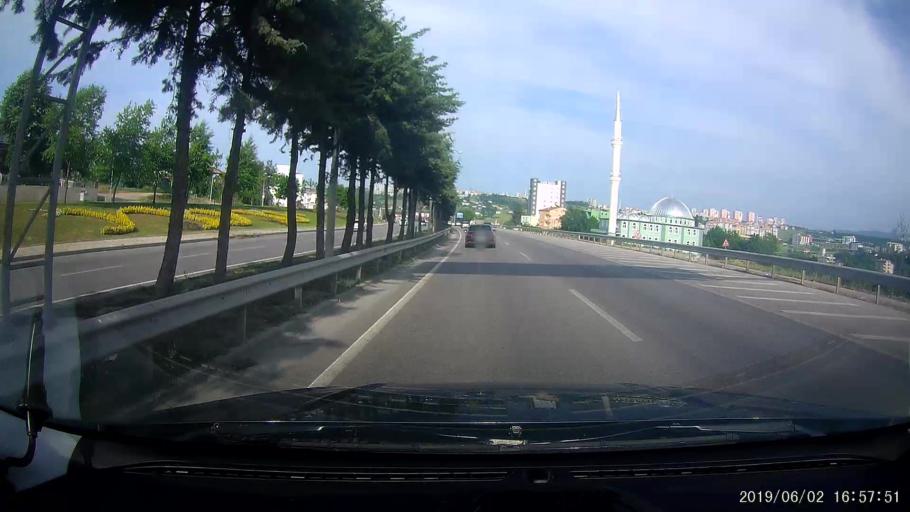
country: TR
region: Samsun
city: Samsun
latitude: 41.2902
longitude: 36.2799
